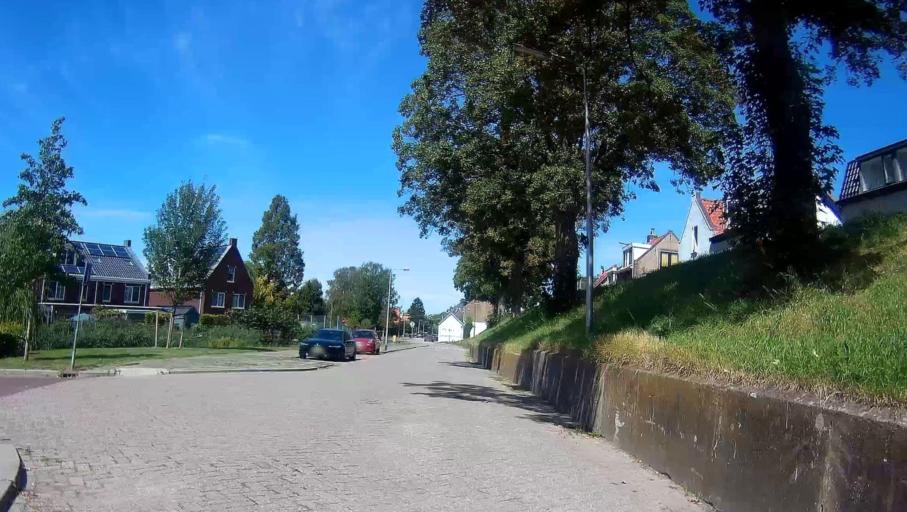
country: NL
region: South Holland
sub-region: Gemeente Ridderkerk
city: Ridderkerk
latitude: 51.8721
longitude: 4.6029
